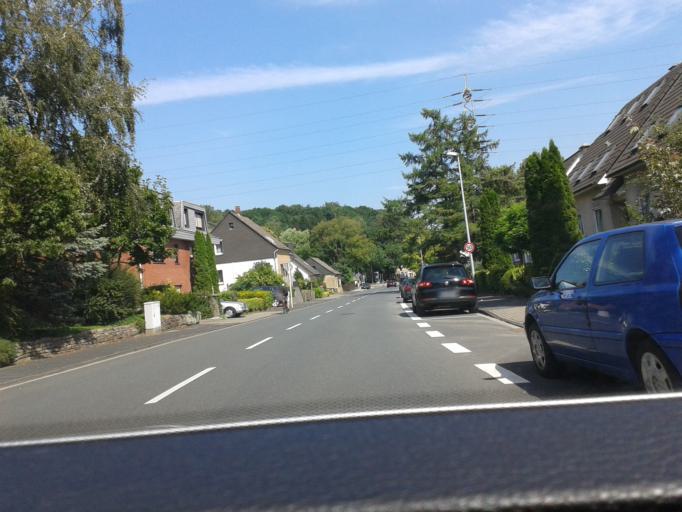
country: DE
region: North Rhine-Westphalia
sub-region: Regierungsbezirk Dusseldorf
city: Muelheim (Ruhr)
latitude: 51.4035
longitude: 6.8573
